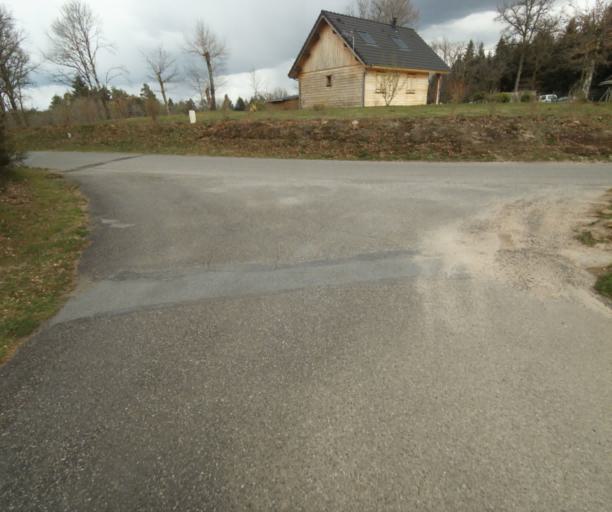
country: FR
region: Limousin
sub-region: Departement de la Correze
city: Correze
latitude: 45.2853
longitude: 1.9693
